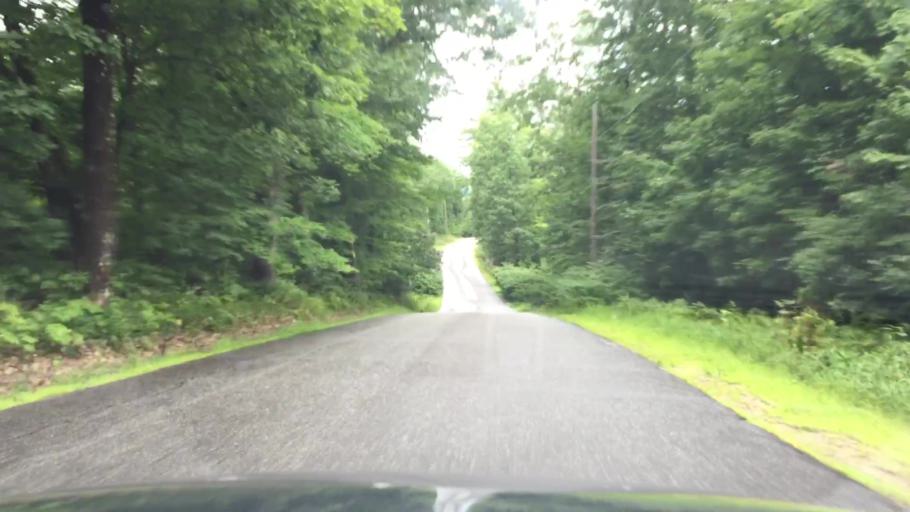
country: US
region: New Hampshire
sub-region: Carroll County
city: Center Harbor
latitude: 43.7180
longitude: -71.4818
